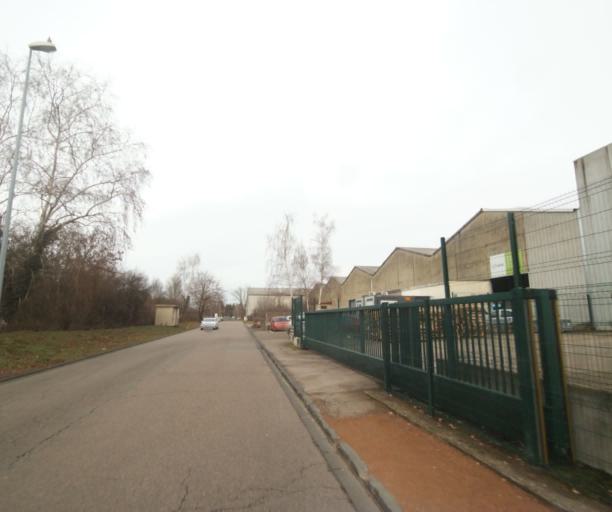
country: FR
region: Rhone-Alpes
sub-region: Departement de la Loire
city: Roanne
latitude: 46.0575
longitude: 4.0795
